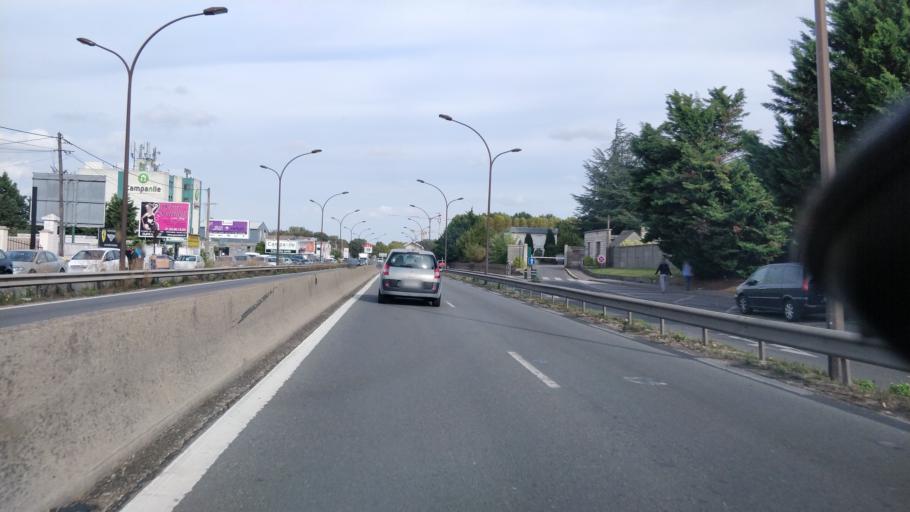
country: FR
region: Ile-de-France
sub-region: Departement de Seine-Saint-Denis
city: Vaujours
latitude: 48.9313
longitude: 2.5566
